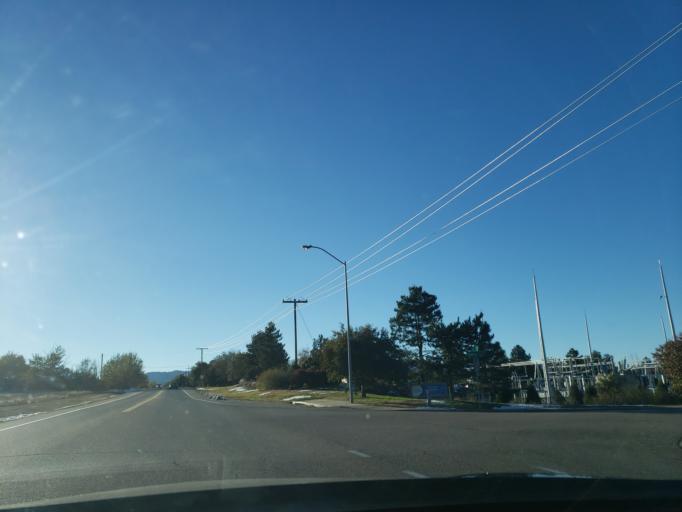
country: US
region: Colorado
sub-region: Larimer County
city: Fort Collins
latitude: 40.4948
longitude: -105.0662
